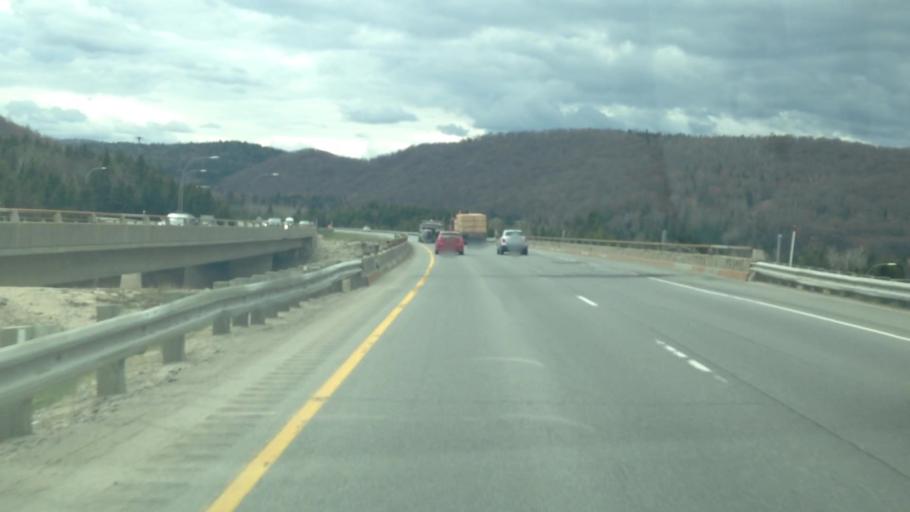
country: CA
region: Quebec
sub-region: Laurentides
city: Val-David
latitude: 45.9904
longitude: -74.1948
